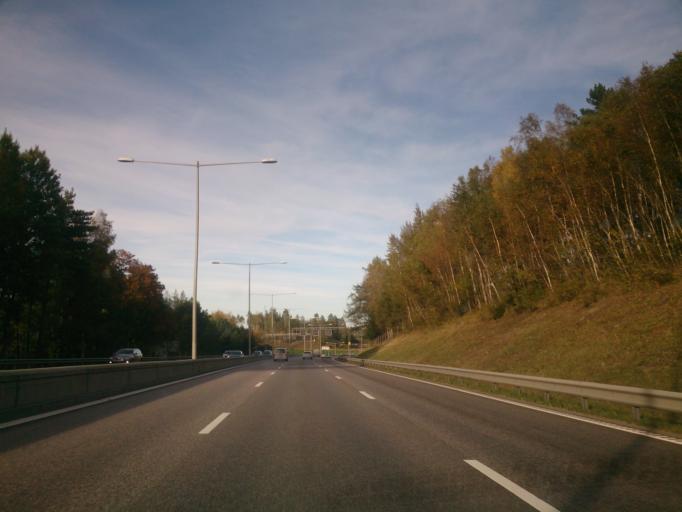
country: SE
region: Stockholm
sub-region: Botkyrka Kommun
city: Eriksberg
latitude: 59.2226
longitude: 17.7845
